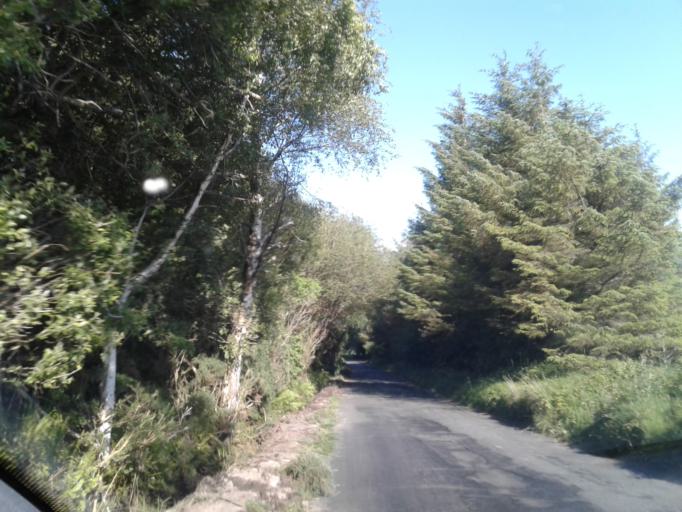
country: IE
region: Leinster
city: Ballinteer
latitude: 53.1951
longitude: -6.2774
